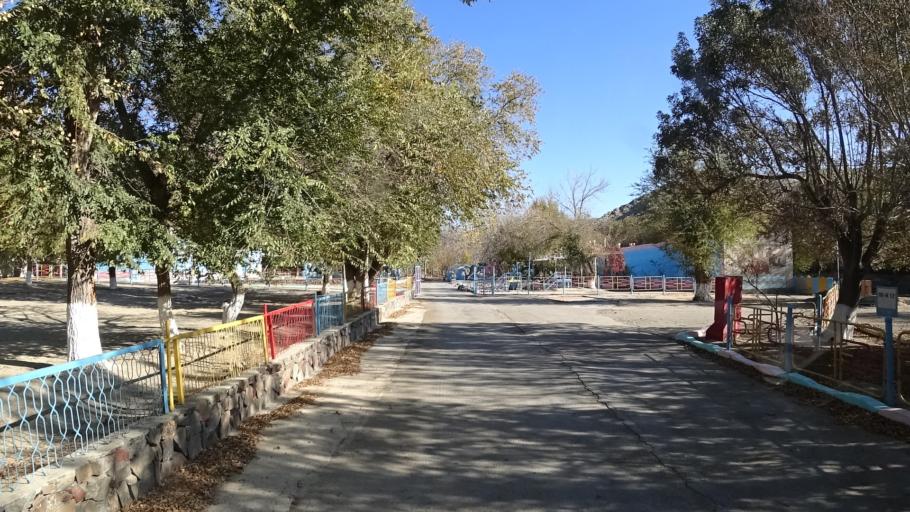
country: UZ
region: Navoiy
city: Karmana Shahri
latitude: 40.2947
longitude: 65.6032
